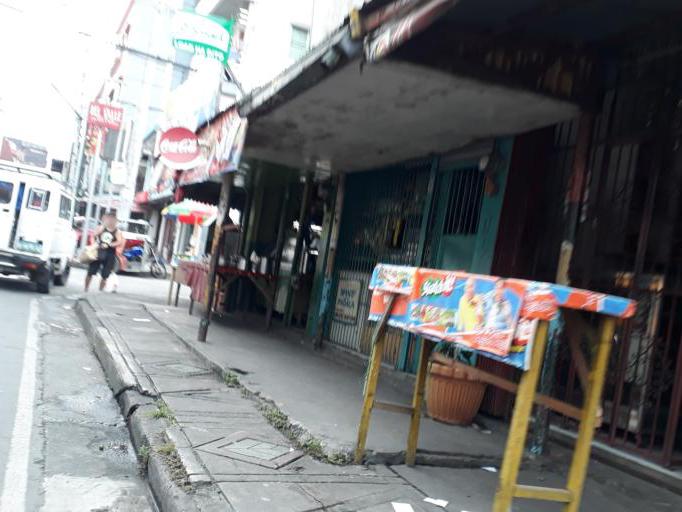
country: PH
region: Metro Manila
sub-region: City of Manila
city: Manila
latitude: 14.6115
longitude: 121.0055
